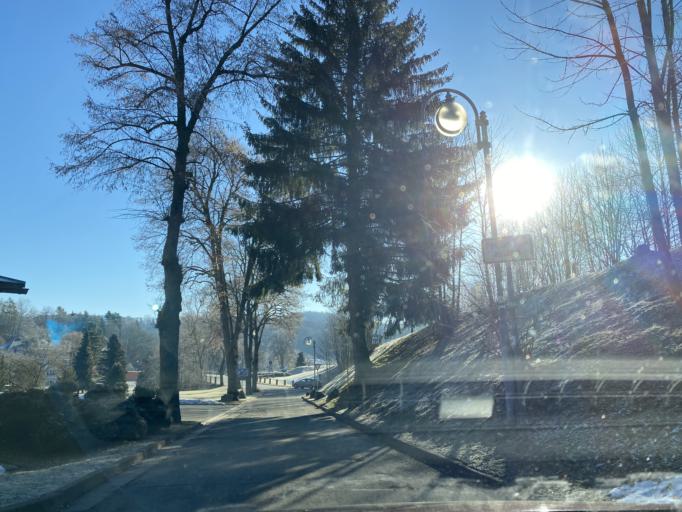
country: DE
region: Saxony
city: Thermalbad Wiesenbad
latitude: 50.6202
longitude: 13.0418
